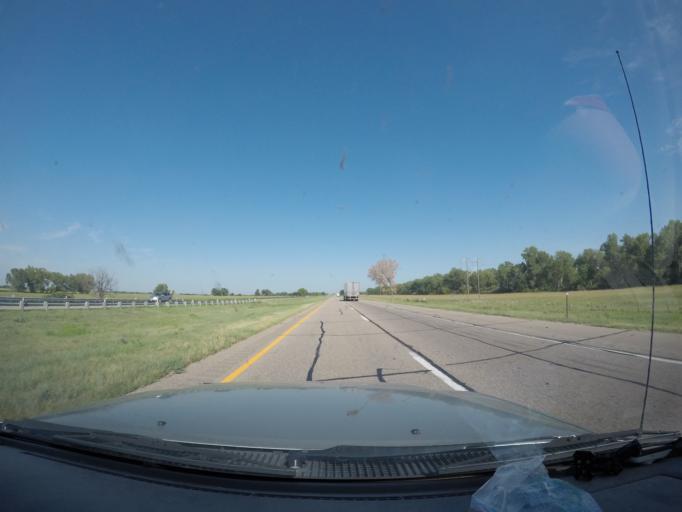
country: US
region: Nebraska
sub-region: Buffalo County
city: Kearney
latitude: 40.6840
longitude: -99.3125
